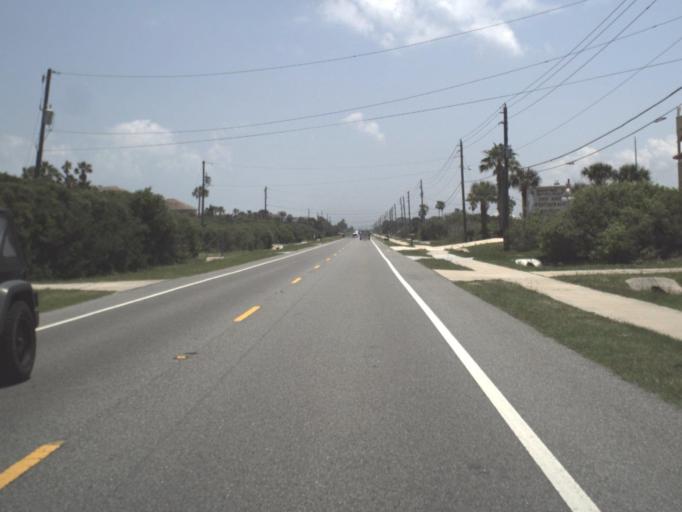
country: US
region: Florida
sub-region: Saint Johns County
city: Butler Beach
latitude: 29.7509
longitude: -81.2467
